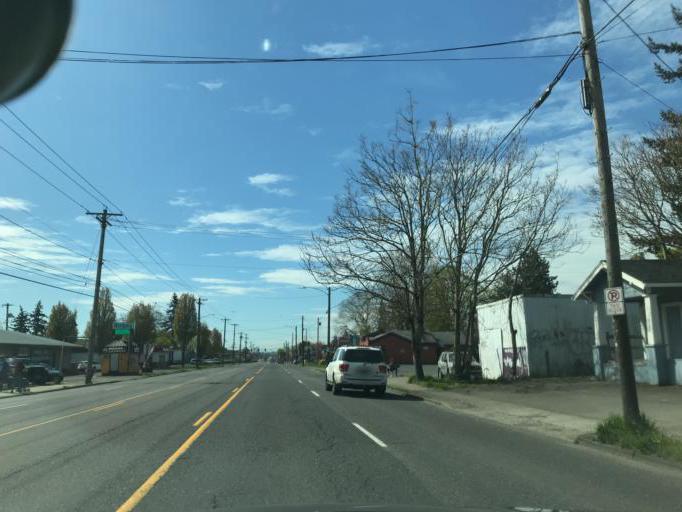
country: US
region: Oregon
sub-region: Multnomah County
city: Lents
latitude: 45.4715
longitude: -122.5791
